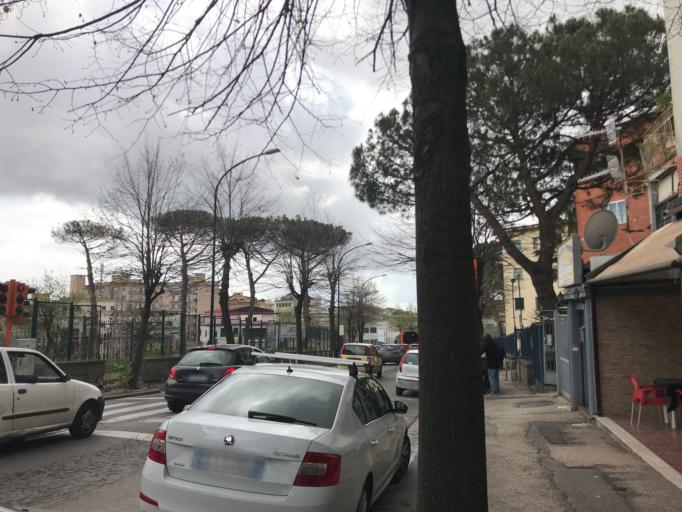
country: IT
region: Campania
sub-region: Provincia di Napoli
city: Napoli
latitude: 40.8571
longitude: 14.2250
